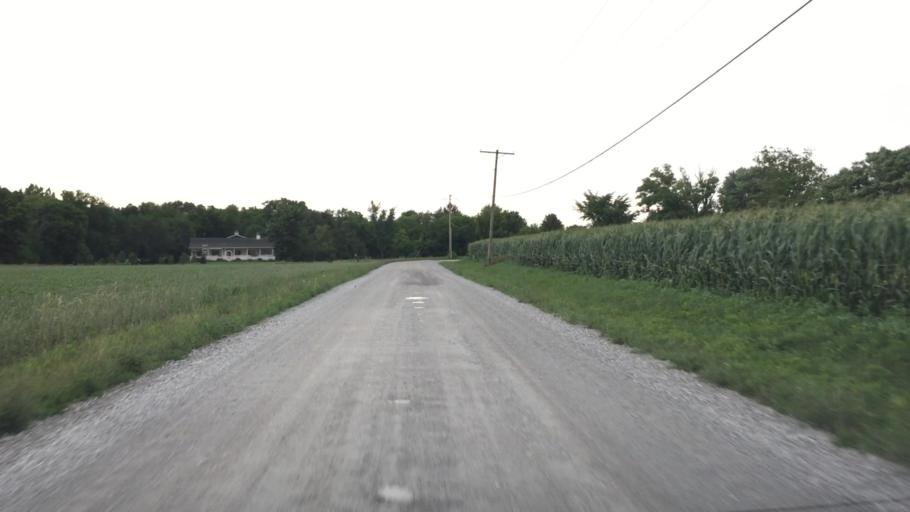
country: US
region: Illinois
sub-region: Hancock County
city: Hamilton
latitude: 40.3743
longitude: -91.3614
